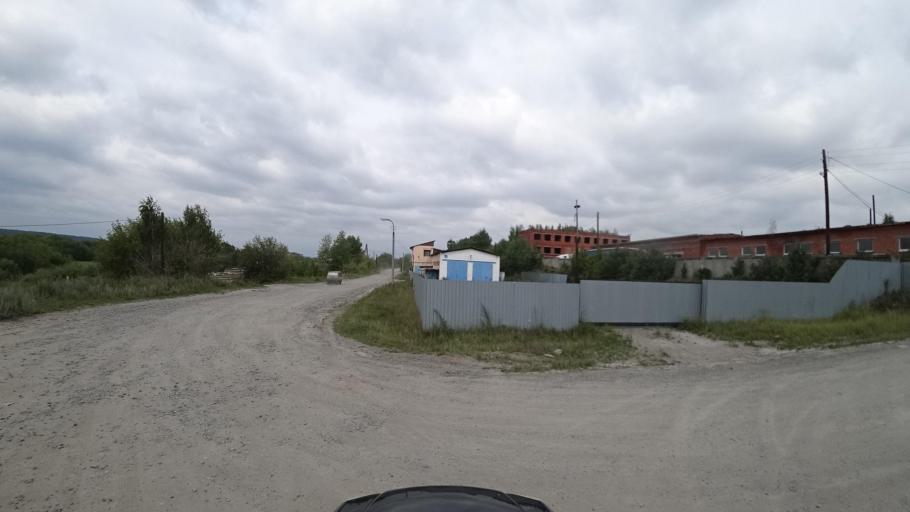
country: RU
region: Sverdlovsk
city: Kamyshlov
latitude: 56.8289
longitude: 62.7301
